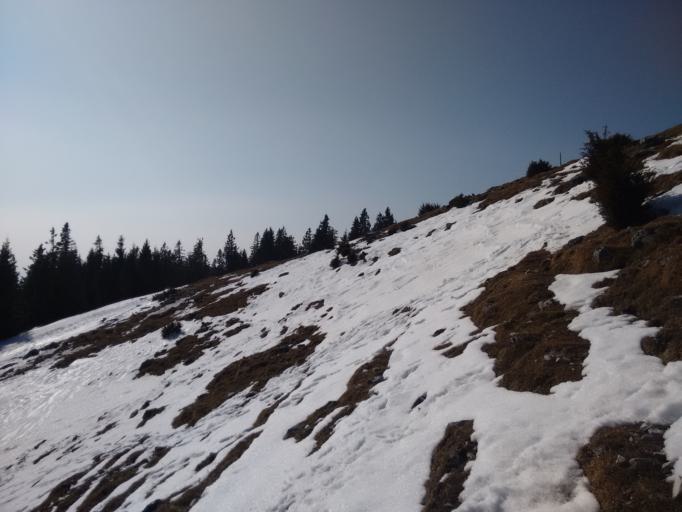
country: AT
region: Styria
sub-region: Politischer Bezirk Graz-Umgebung
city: Sankt Radegund bei Graz
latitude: 47.1972
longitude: 15.4658
